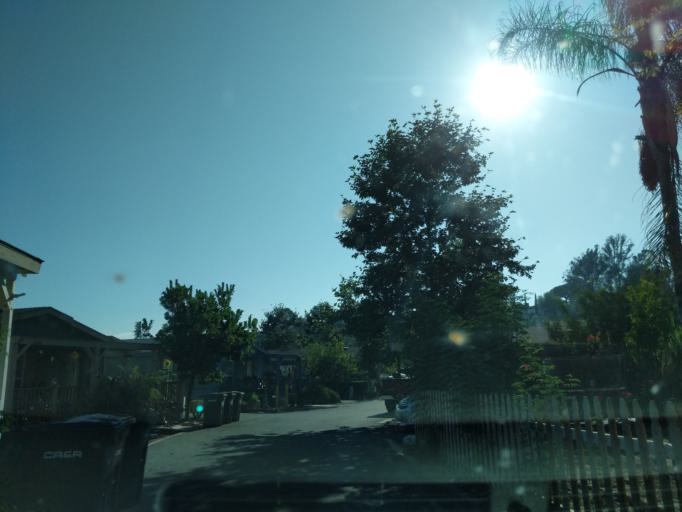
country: US
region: California
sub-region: Orange County
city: San Juan Capistrano
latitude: 33.5033
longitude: -117.6667
